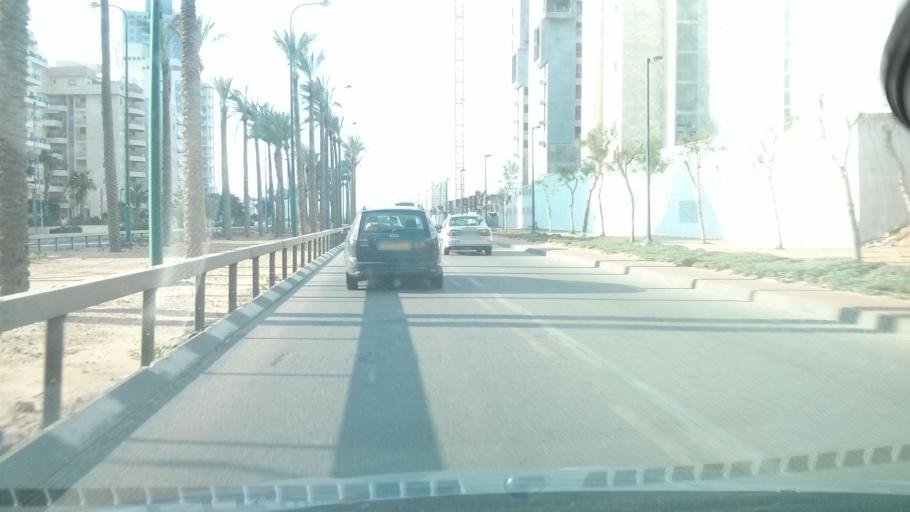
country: IL
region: Central District
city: Netanya
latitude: 32.2966
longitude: 34.8435
